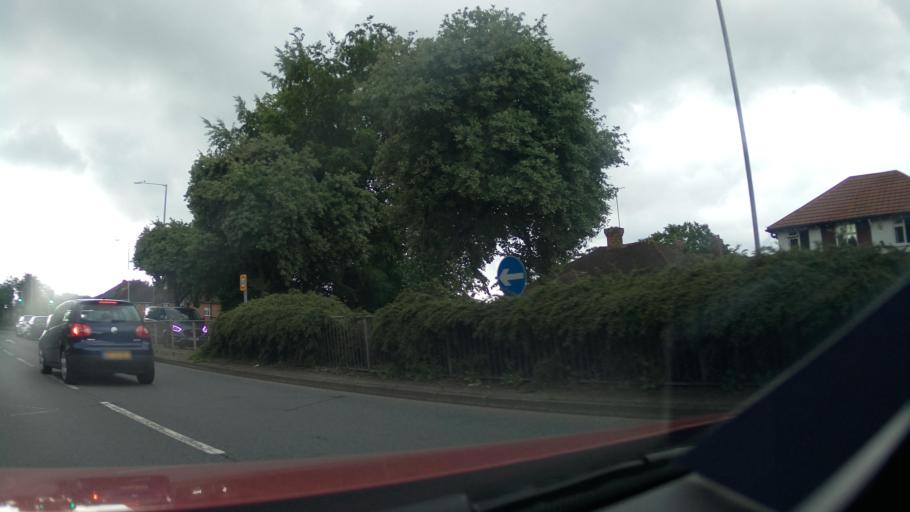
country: GB
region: England
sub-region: Wolverhampton
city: Wolverhampton
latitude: 52.5596
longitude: -2.1582
